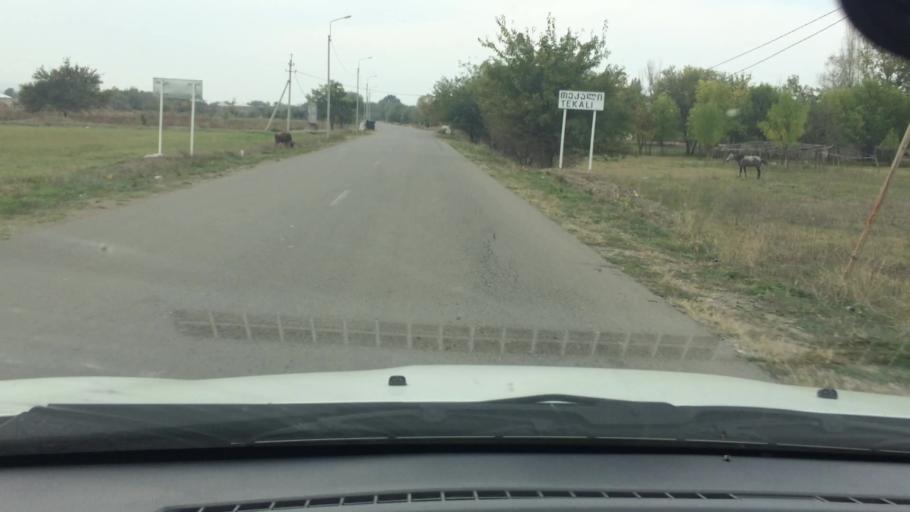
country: AM
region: Tavush
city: Berdavan
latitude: 41.3477
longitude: 44.9781
